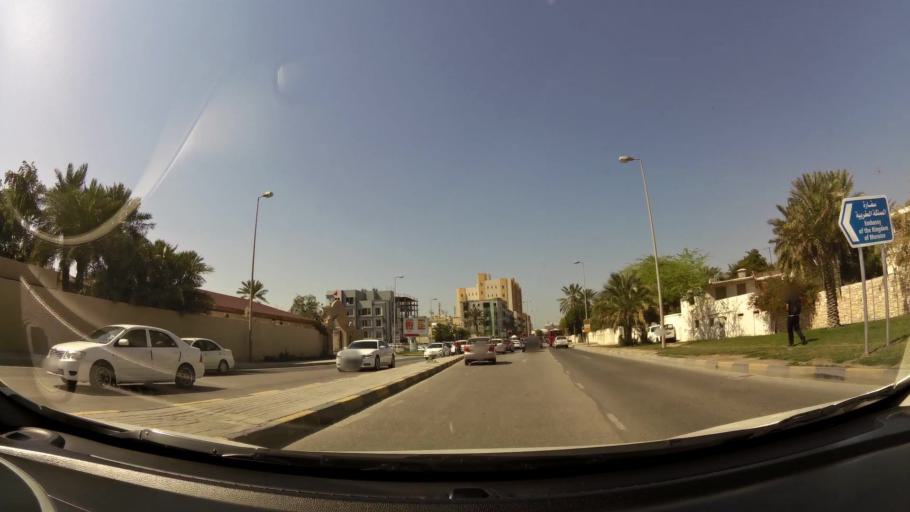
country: BH
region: Manama
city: Manama
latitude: 26.2133
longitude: 50.5824
